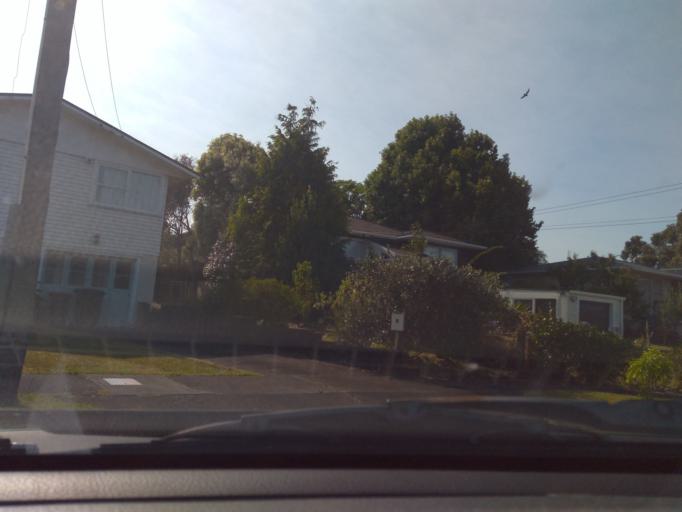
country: NZ
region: Auckland
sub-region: Auckland
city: Waitakere
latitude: -36.9214
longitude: 174.6939
